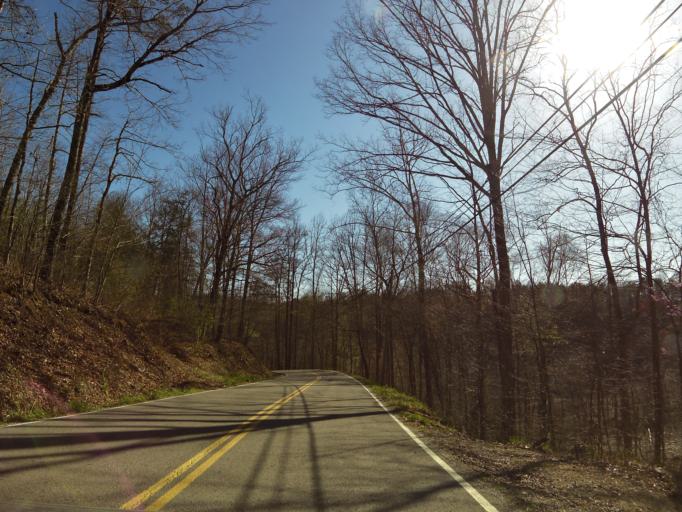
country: US
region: Tennessee
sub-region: Scott County
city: Huntsville
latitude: 36.3516
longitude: -84.3885
